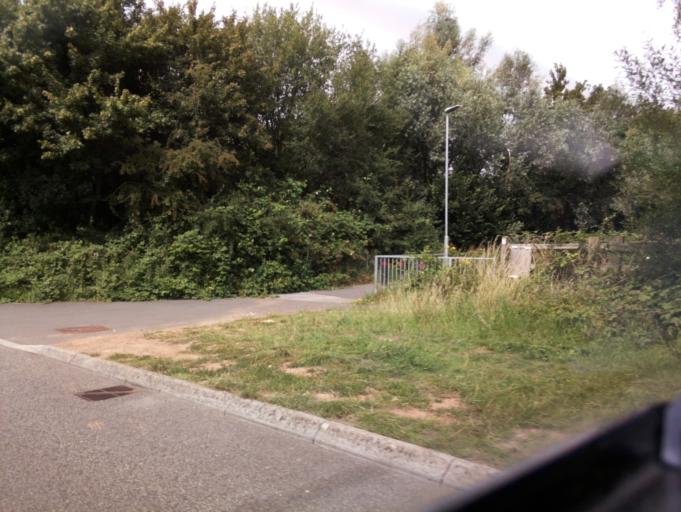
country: GB
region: England
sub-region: Somerset
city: Glastonbury
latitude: 51.1585
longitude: -2.7128
